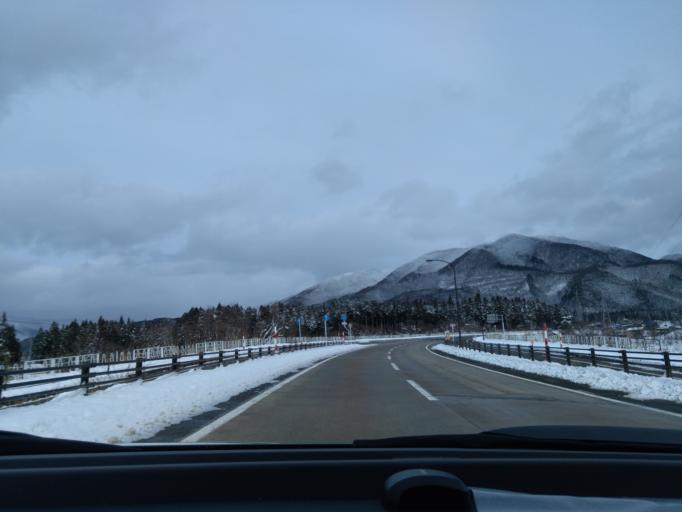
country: JP
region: Akita
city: Kakunodatemachi
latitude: 39.6990
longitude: 140.7321
